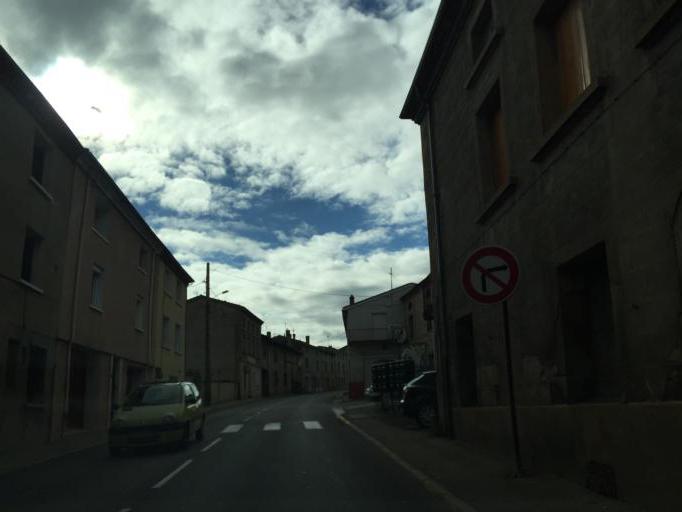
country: FR
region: Rhone-Alpes
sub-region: Departement de la Loire
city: Saint-Paul-en-Jarez
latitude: 45.4816
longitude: 4.5780
